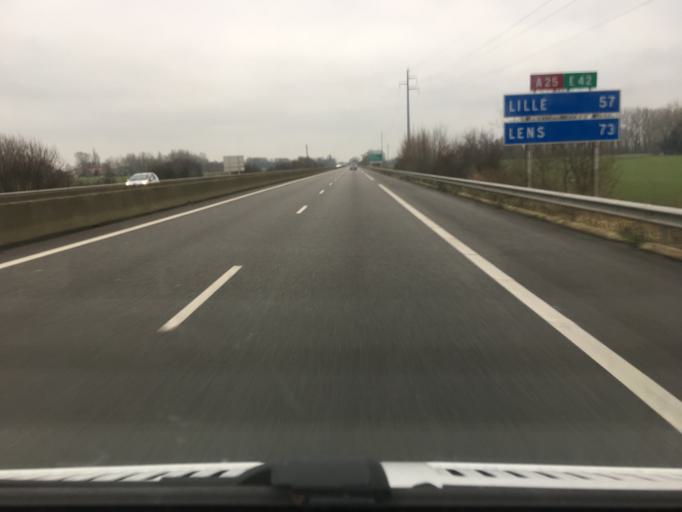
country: FR
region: Nord-Pas-de-Calais
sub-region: Departement du Nord
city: Herzeele
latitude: 50.8762
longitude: 2.5239
